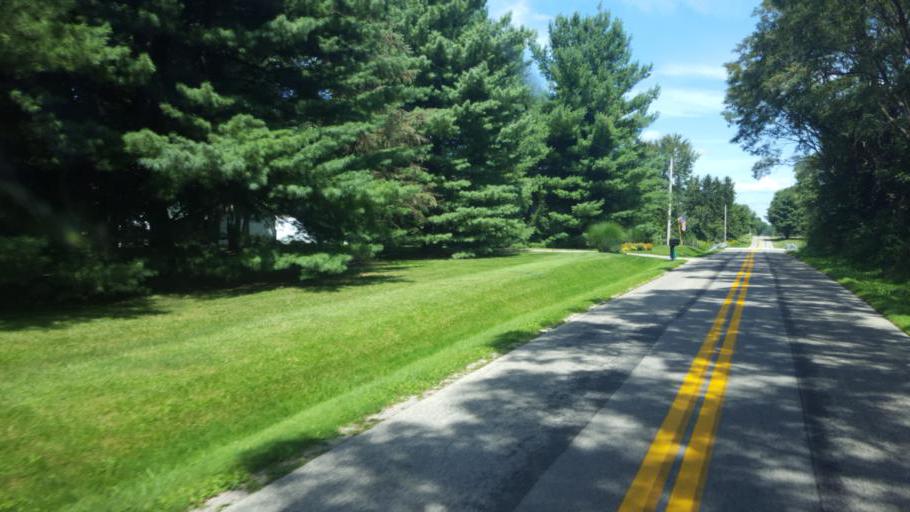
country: US
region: Ohio
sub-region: Delaware County
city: Sunbury
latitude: 40.2864
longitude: -82.8058
